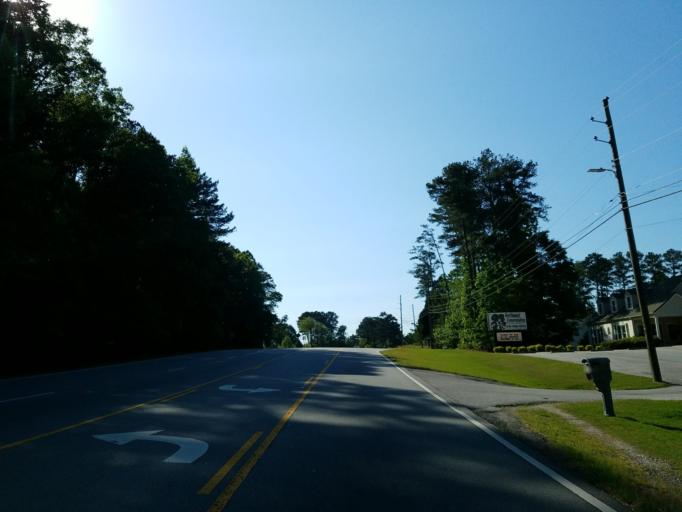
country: US
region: Georgia
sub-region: Paulding County
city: Dallas
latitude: 33.9127
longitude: -84.8226
